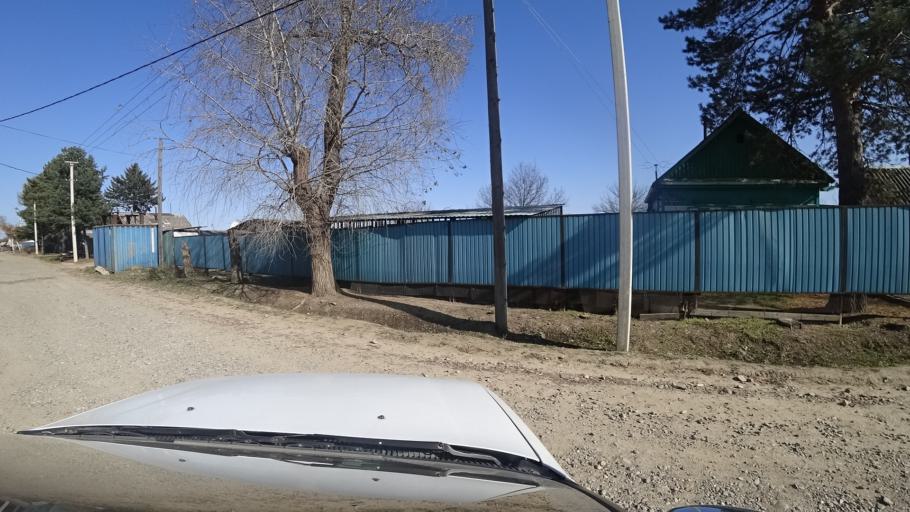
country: RU
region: Primorskiy
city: Dal'nerechensk
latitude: 45.9279
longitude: 133.7530
